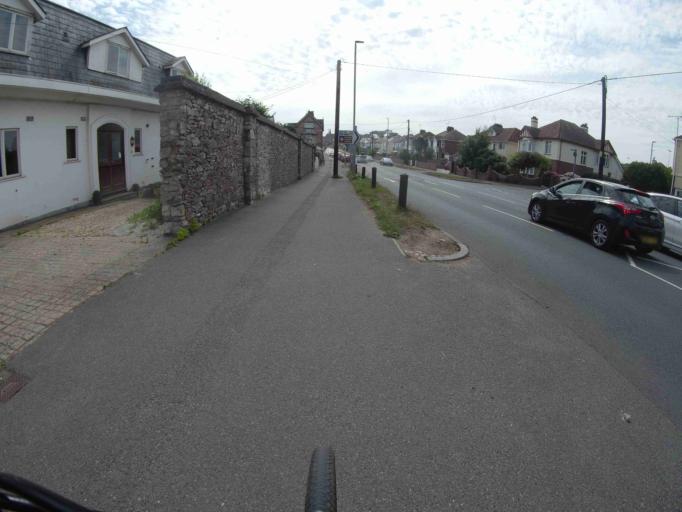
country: GB
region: England
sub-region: Devon
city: Dawlish
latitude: 50.5857
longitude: -3.4586
